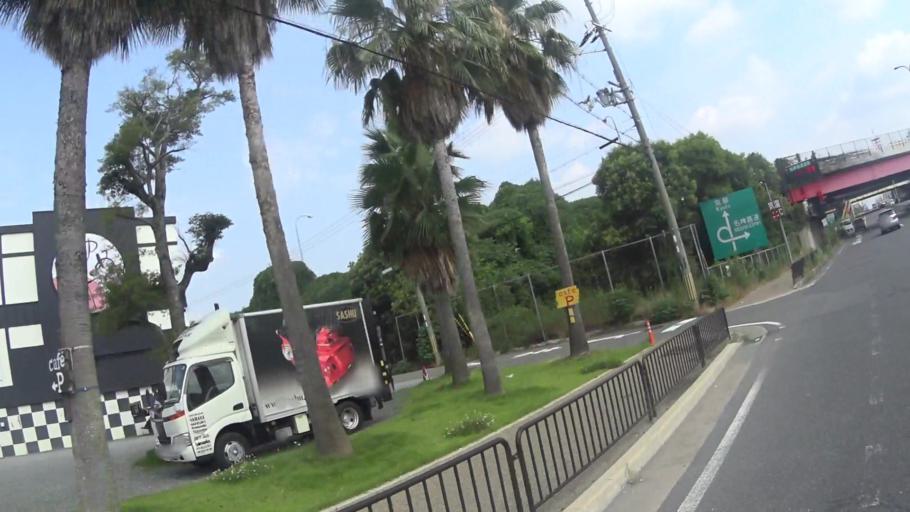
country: JP
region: Kyoto
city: Muko
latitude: 34.9521
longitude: 135.7454
